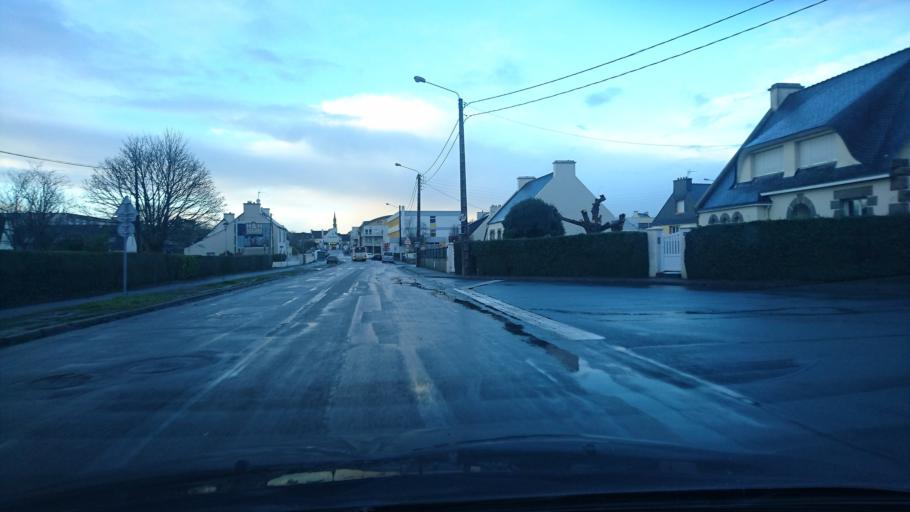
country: FR
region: Brittany
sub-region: Departement du Finistere
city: Guilers
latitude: 48.4217
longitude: -4.5584
